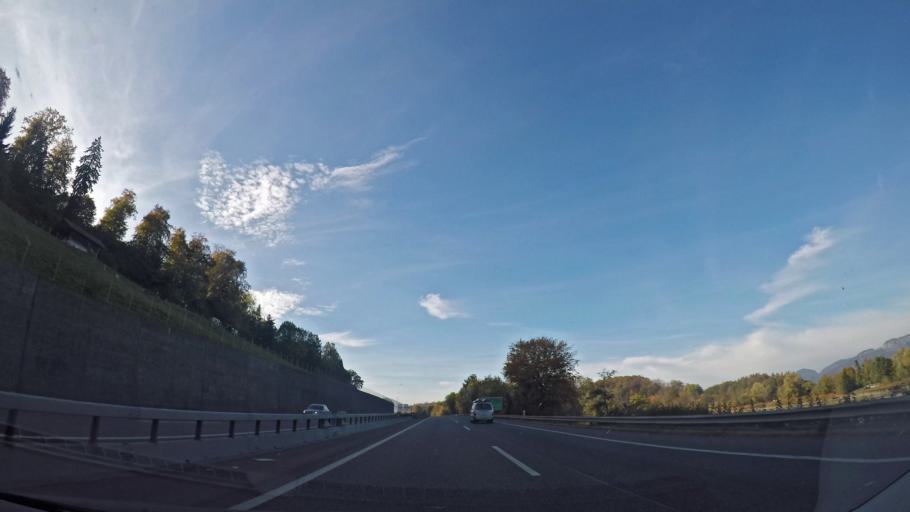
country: CH
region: Bern
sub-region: Frutigen-Niedersimmental District
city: Wimmis
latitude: 46.6881
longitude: 7.6640
